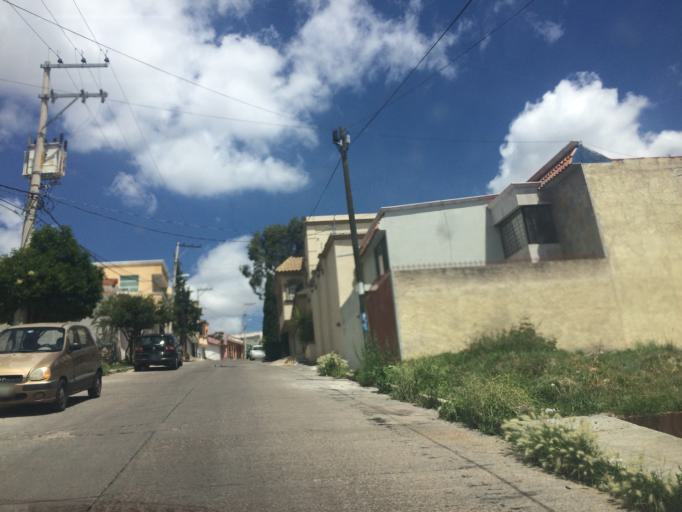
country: MX
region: Zacatecas
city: Zacatecas
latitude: 22.7560
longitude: -102.5785
